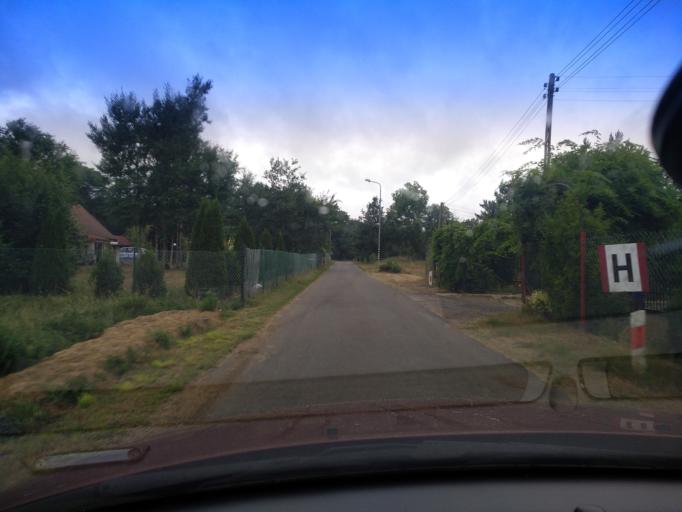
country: PL
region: Lower Silesian Voivodeship
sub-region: Powiat zgorzelecki
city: Wegliniec
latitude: 51.2619
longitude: 15.1968
